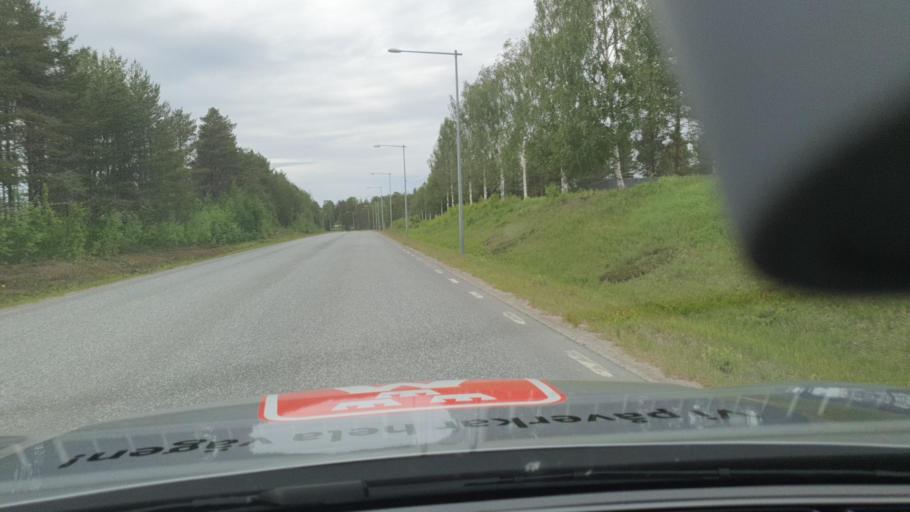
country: SE
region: Norrbotten
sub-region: Kalix Kommun
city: Rolfs
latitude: 65.8650
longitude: 23.1342
